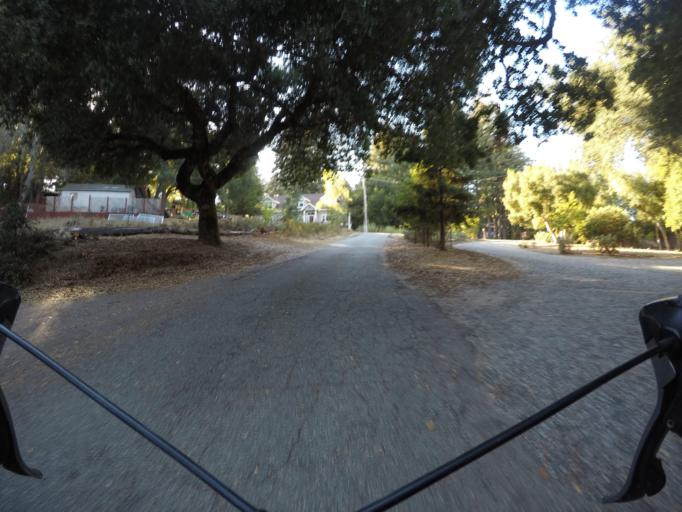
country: US
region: California
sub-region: Santa Cruz County
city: Brookdale
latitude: 37.1147
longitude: -122.1025
